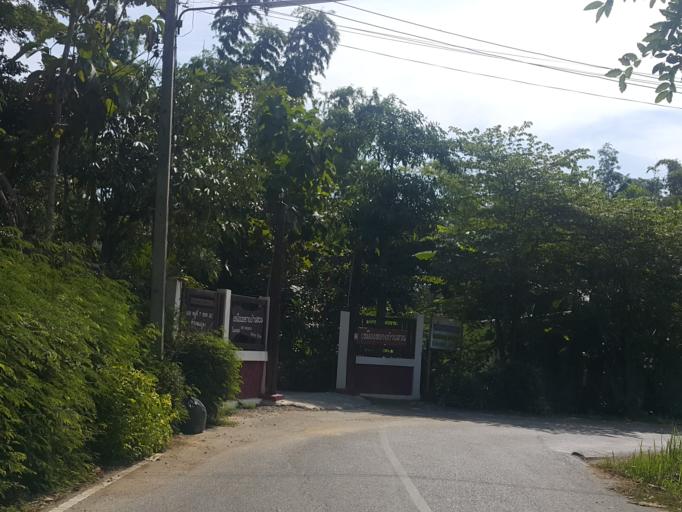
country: TH
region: Chiang Mai
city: San Kamphaeng
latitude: 18.7691
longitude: 99.1088
